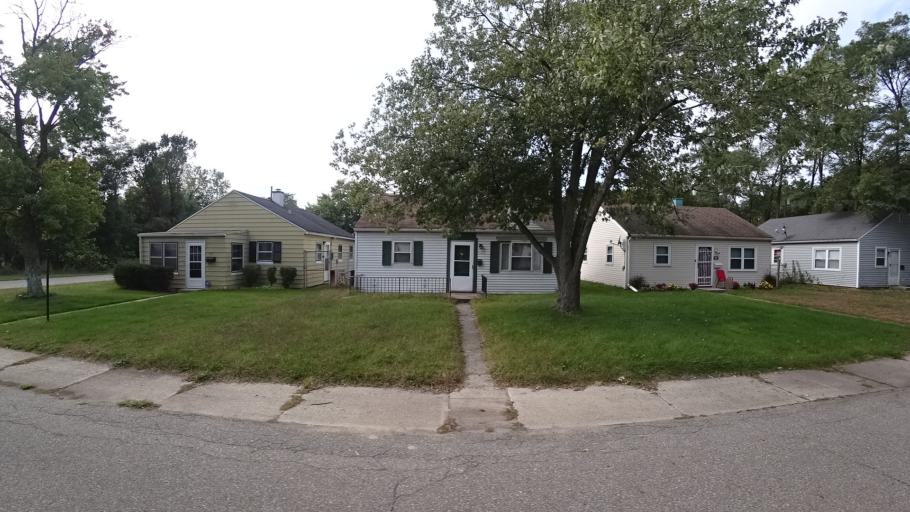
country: US
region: Indiana
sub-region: LaPorte County
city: Trail Creek
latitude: 41.7159
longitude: -86.8708
